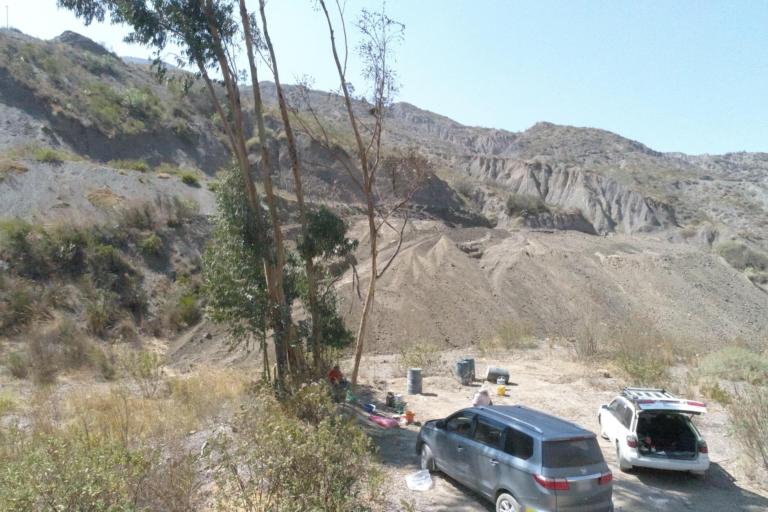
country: BO
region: La Paz
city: La Paz
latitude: -16.6221
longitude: -68.0416
